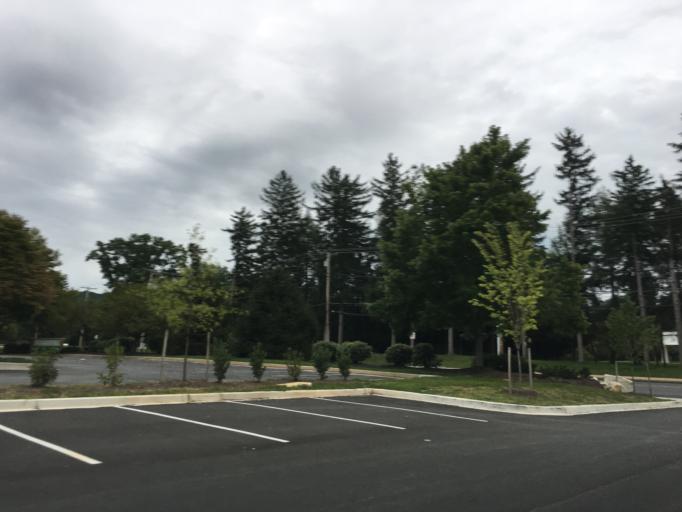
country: US
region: Maryland
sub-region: Baltimore County
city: Cockeysville
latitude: 39.4895
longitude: -76.6504
